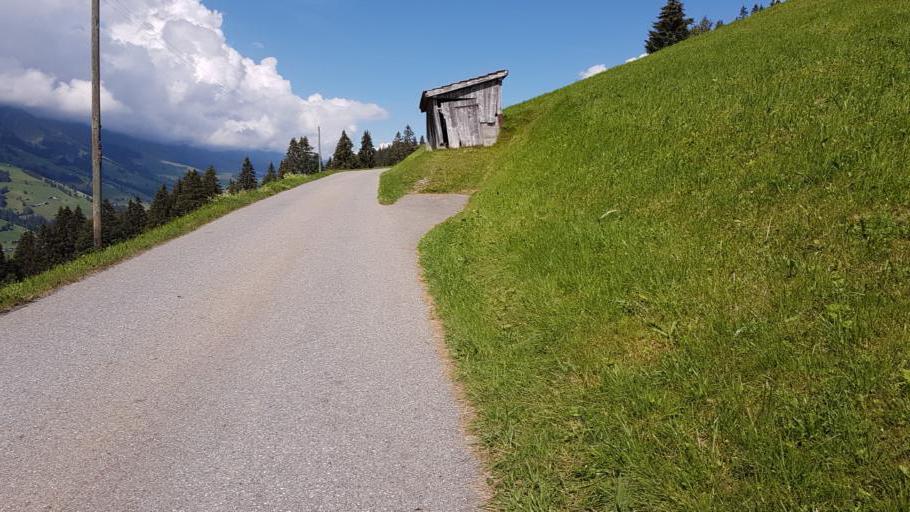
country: CH
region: Bern
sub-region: Frutigen-Niedersimmental District
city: Adelboden
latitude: 46.5049
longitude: 7.5900
